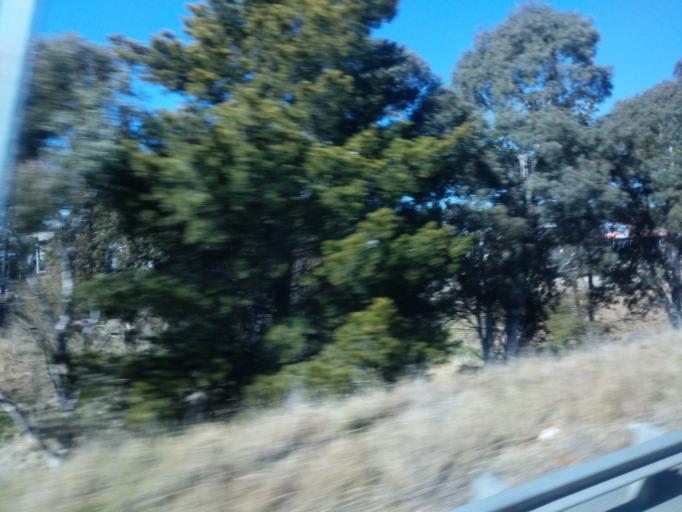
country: AU
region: Australian Capital Territory
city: Forrest
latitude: -35.3277
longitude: 149.1626
